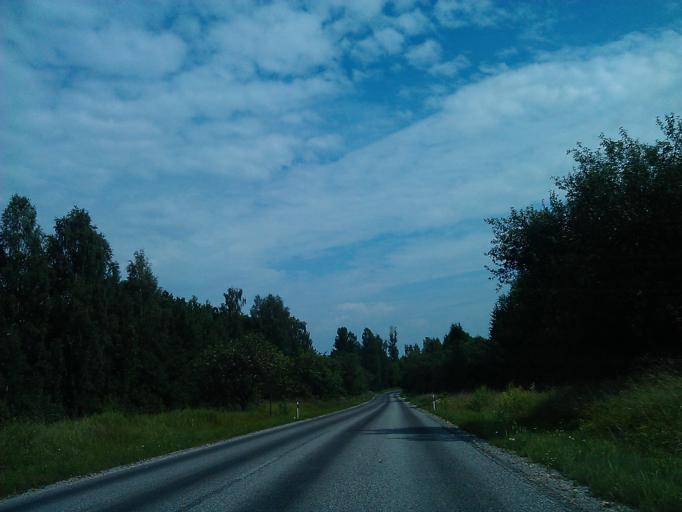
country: LV
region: Priekuli
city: Priekuli
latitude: 57.3496
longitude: 25.3490
